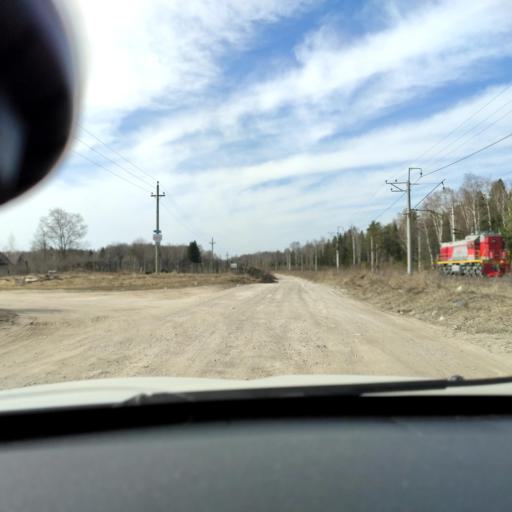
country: RU
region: Perm
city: Overyata
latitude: 58.0577
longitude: 55.9918
